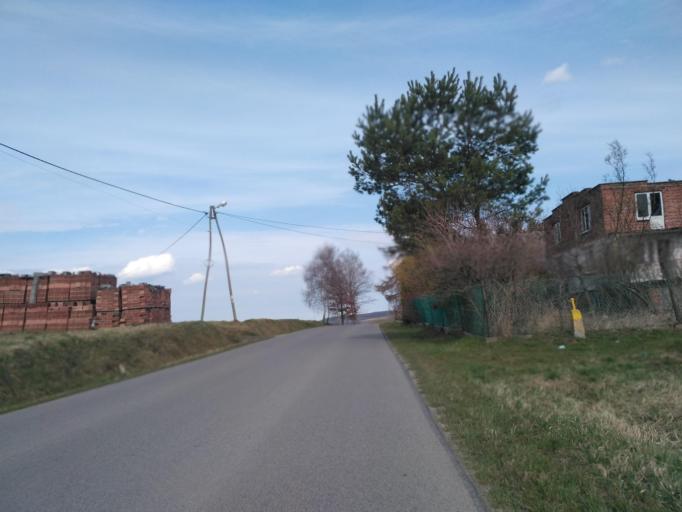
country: PL
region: Subcarpathian Voivodeship
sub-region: Powiat ropczycko-sedziszowski
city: Iwierzyce
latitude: 50.0062
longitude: 21.7911
